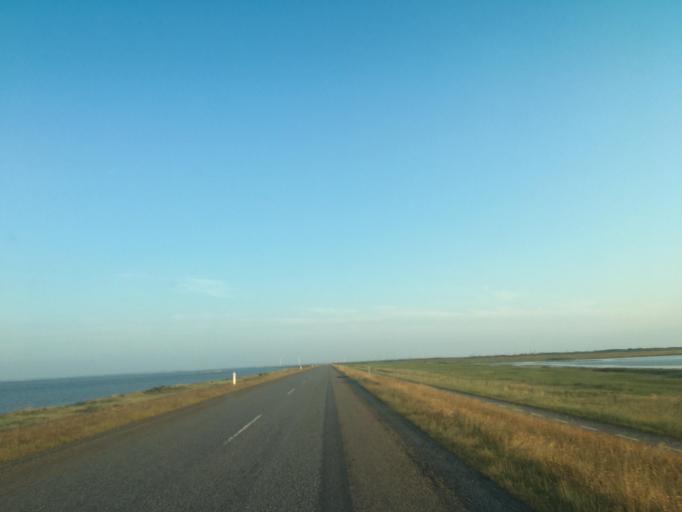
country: DK
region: Central Jutland
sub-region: Lemvig Kommune
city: Thyboron
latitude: 56.7394
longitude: 8.2504
